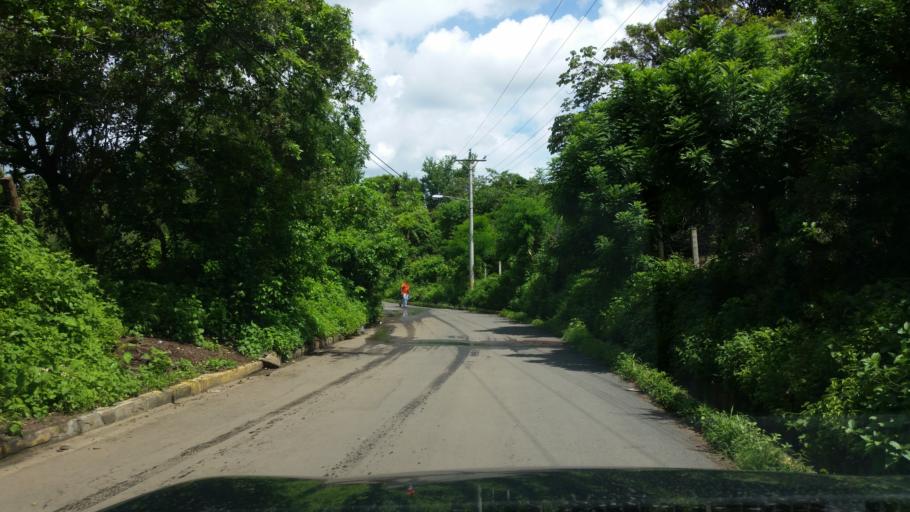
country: NI
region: Managua
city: Managua
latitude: 12.0857
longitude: -86.2202
